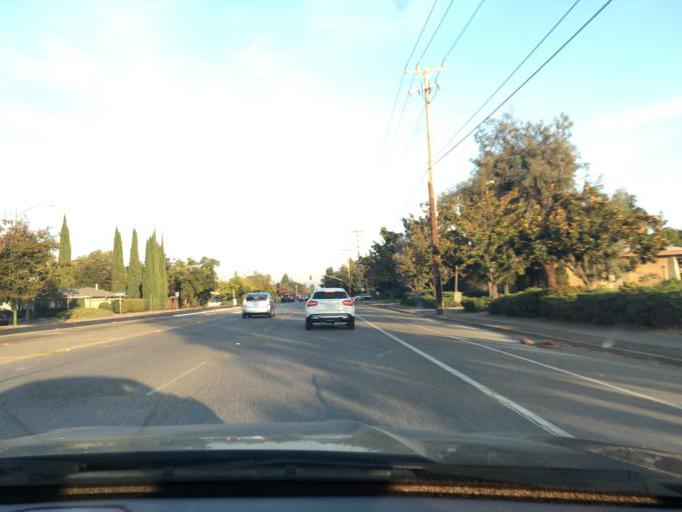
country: US
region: California
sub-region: Santa Clara County
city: Saratoga
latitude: 37.2936
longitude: -122.0168
